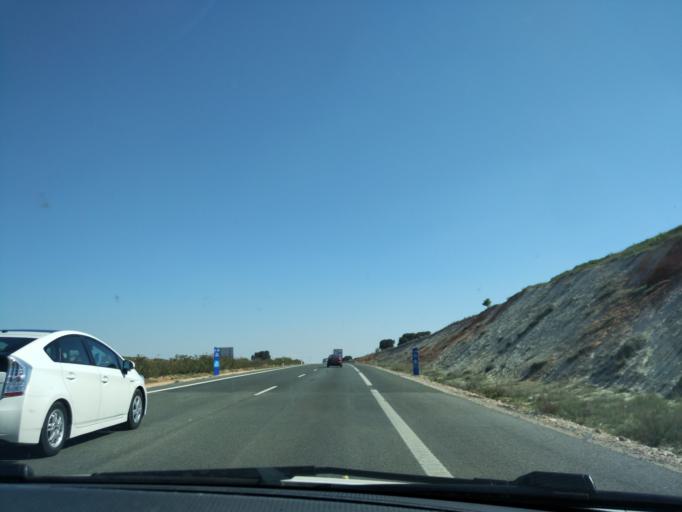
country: ES
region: Castille-La Mancha
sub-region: Provincia de Albacete
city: Pozo-Canada
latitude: 38.7562
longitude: -1.6941
